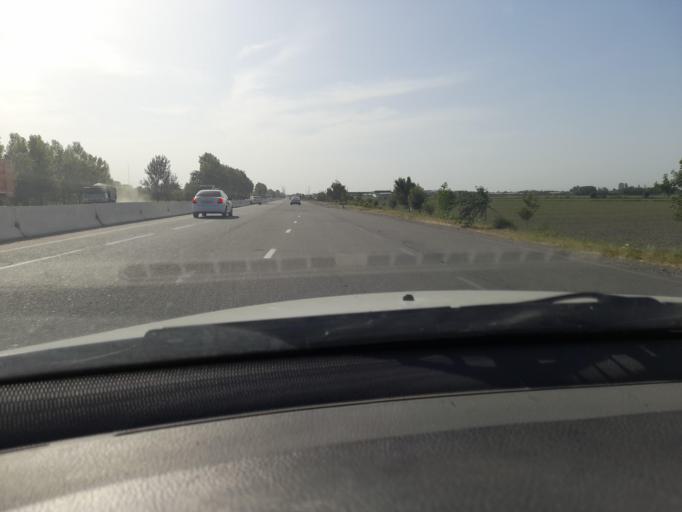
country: UZ
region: Samarqand
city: Kattaqo'rg'on
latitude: 39.9166
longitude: 66.3075
